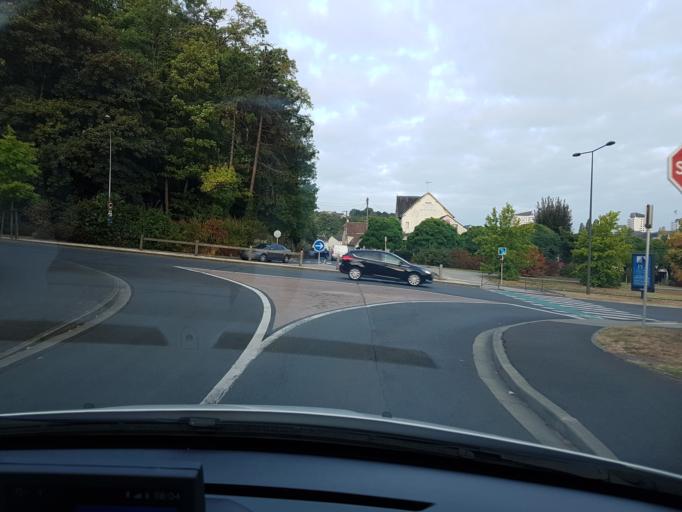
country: FR
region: Centre
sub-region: Departement d'Indre-et-Loire
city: Saint-Avertin
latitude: 47.3656
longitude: 0.7187
